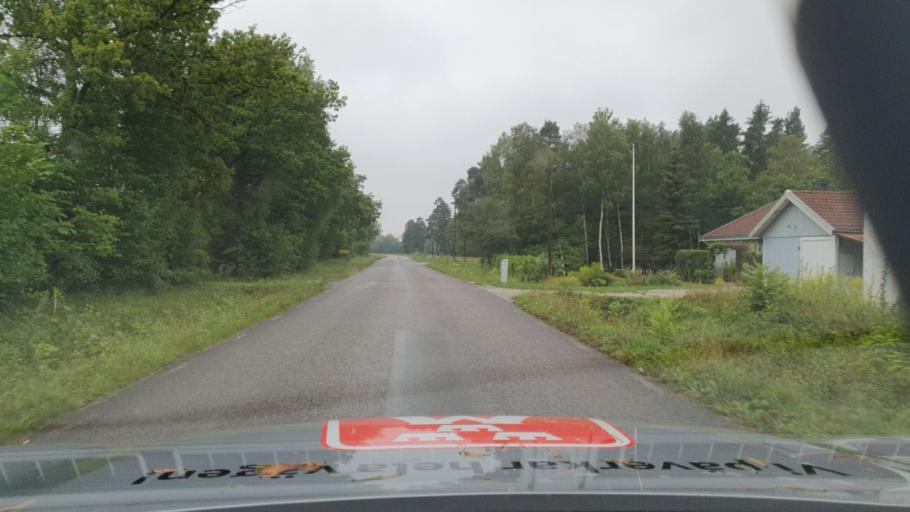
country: SE
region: Gotland
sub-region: Gotland
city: Visby
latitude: 57.7793
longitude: 18.5017
